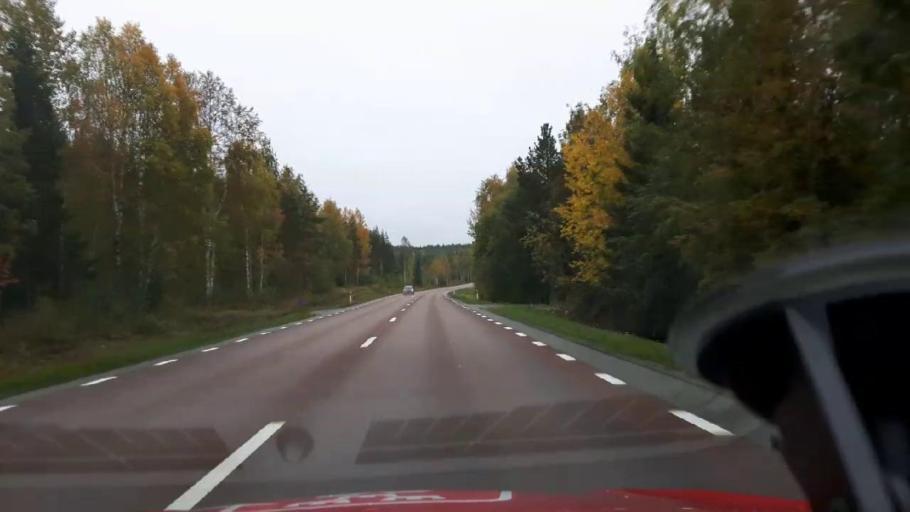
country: SE
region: Jaemtland
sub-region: Bergs Kommun
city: Hoverberg
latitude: 62.8407
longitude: 14.5188
